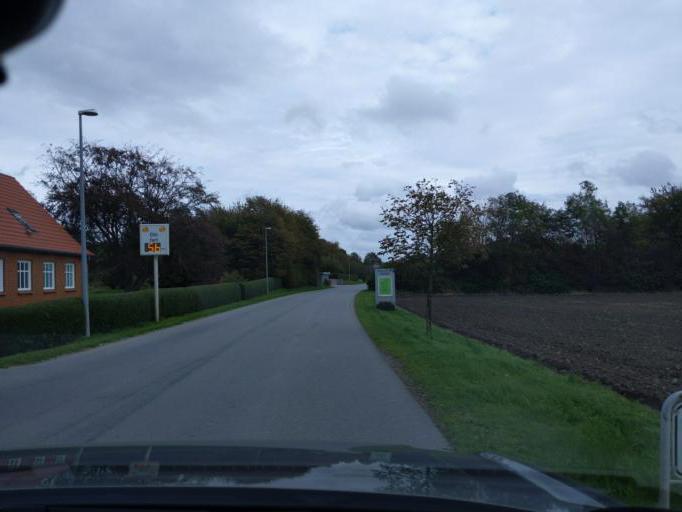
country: DK
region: Central Jutland
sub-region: Viborg Kommune
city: Viborg
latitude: 56.4168
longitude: 9.4889
